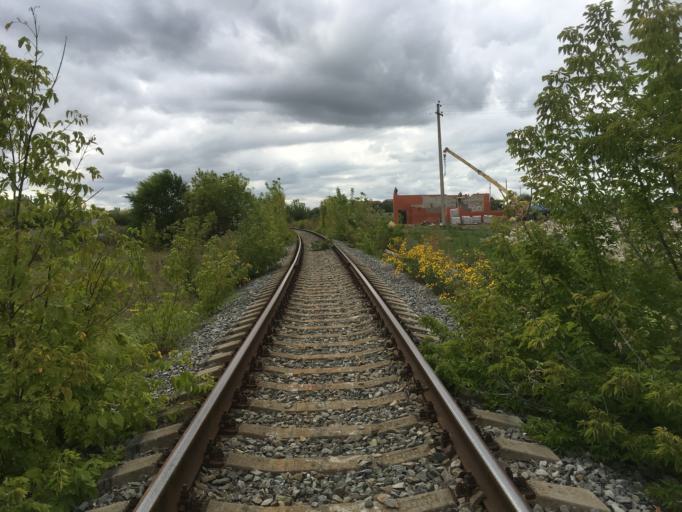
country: RU
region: Voronezj
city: Rossosh'
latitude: 50.2127
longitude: 39.5214
